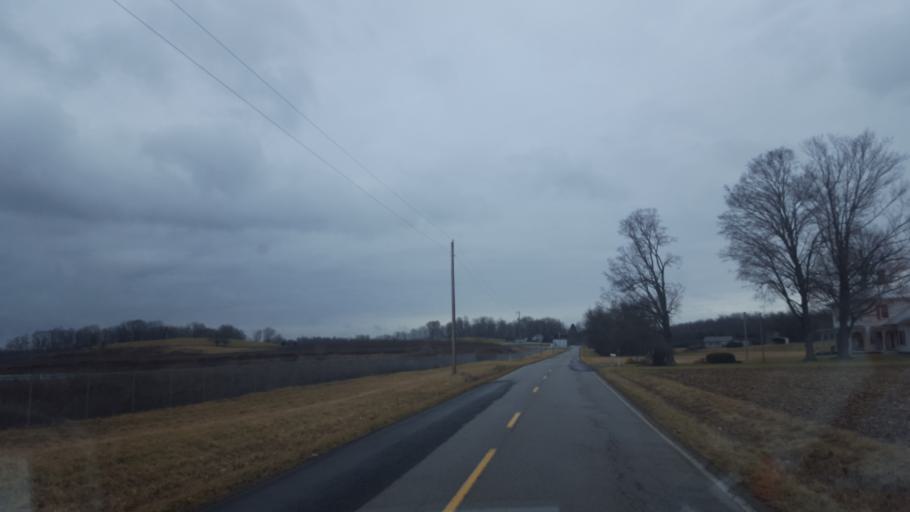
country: US
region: Ohio
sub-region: Knox County
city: Fredericktown
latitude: 40.4553
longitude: -82.5171
